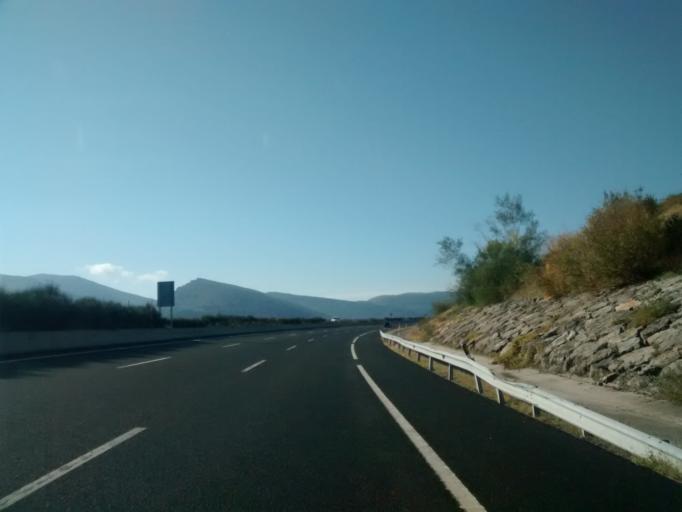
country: ES
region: Cantabria
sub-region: Provincia de Cantabria
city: Molledo
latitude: 43.1434
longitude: -4.0565
